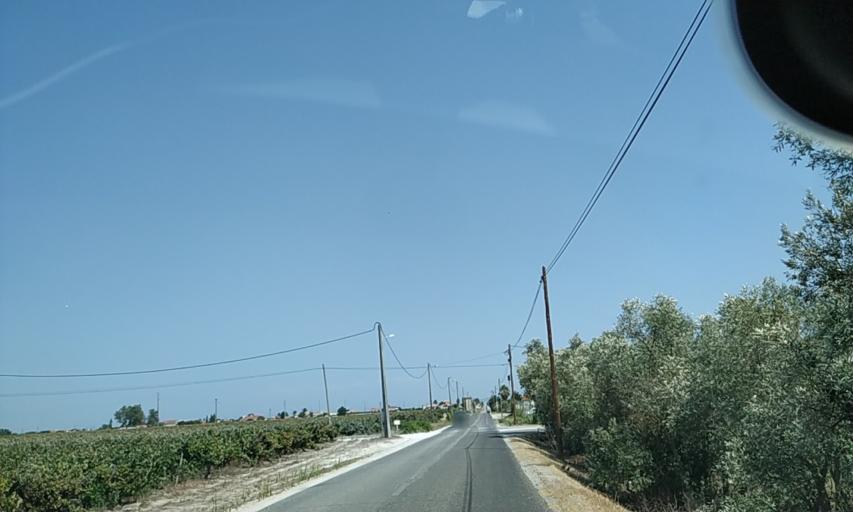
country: PT
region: Setubal
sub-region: Palmela
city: Palmela
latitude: 38.6041
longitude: -8.8253
